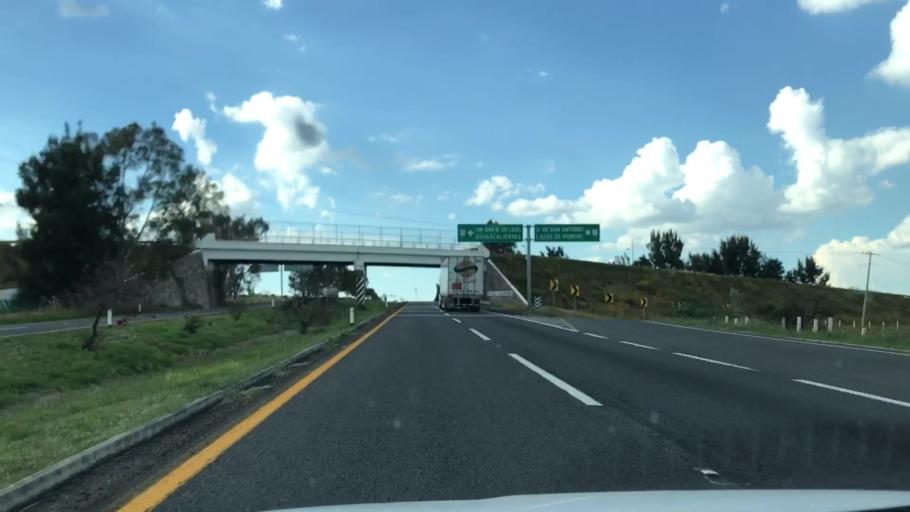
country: MX
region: Jalisco
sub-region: Lagos de Moreno
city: Cristeros [Fraccionamiento]
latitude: 21.2526
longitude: -101.9493
